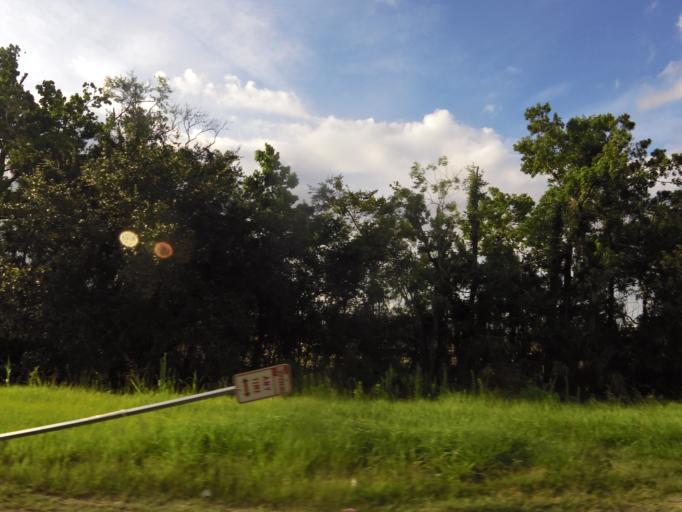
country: US
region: Florida
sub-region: Duval County
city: Jacksonville
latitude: 30.3214
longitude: -81.7464
